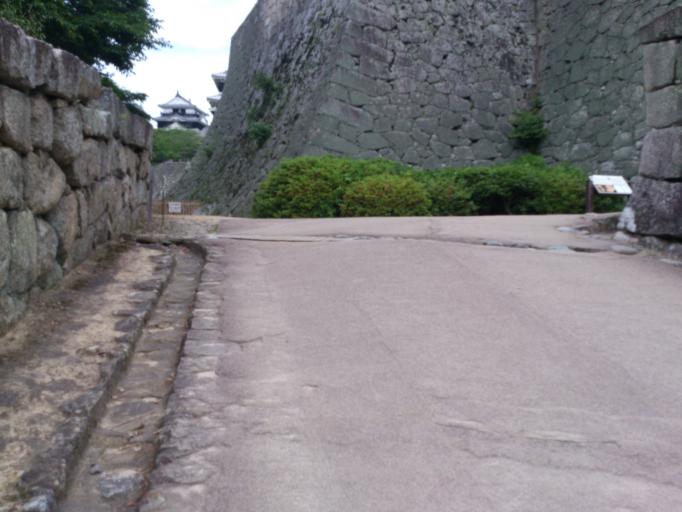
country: JP
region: Ehime
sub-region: Shikoku-chuo Shi
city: Matsuyama
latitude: 33.8436
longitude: 132.7665
